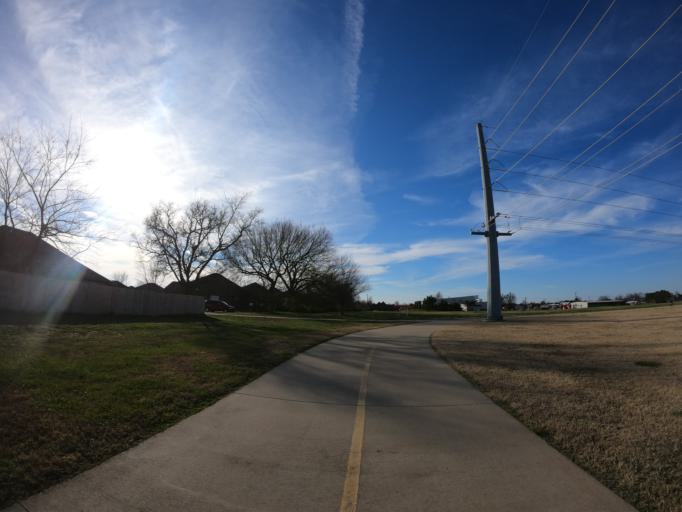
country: US
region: Arkansas
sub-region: Benton County
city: Lowell
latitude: 36.2768
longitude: -94.1693
